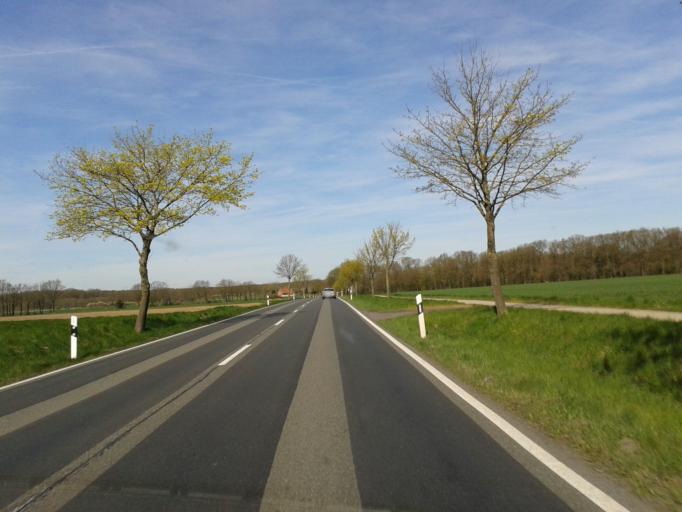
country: DE
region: Lower Saxony
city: Gerdau
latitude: 52.9583
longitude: 10.4264
